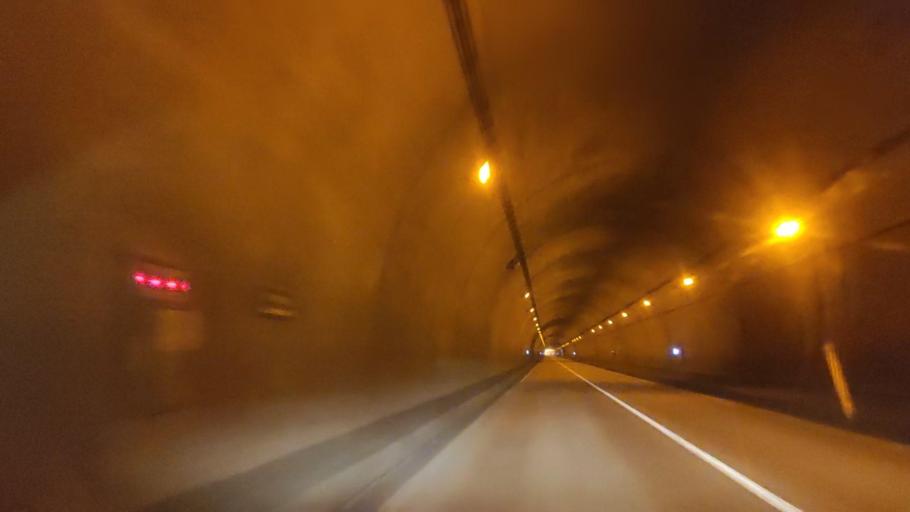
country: JP
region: Hokkaido
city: Date
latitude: 42.5579
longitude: 140.7621
